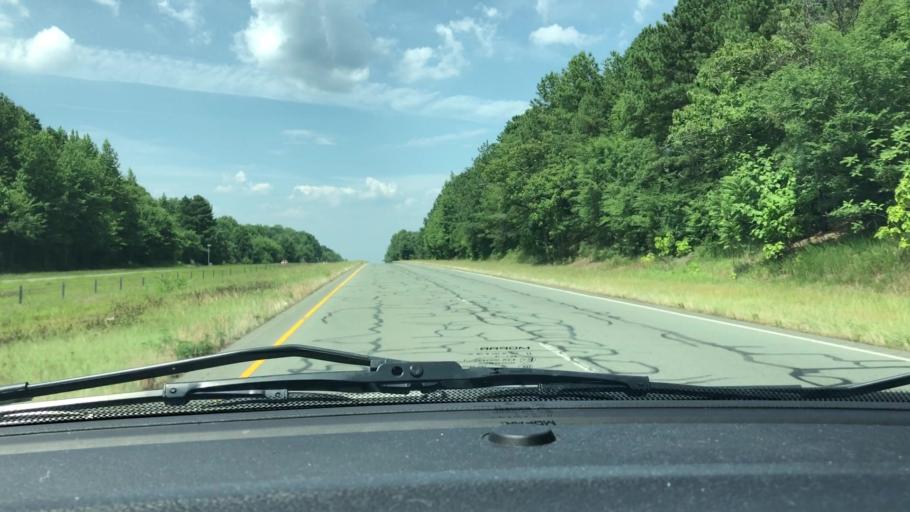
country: US
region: North Carolina
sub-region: Chatham County
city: Siler City
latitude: 35.7093
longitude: -79.4288
